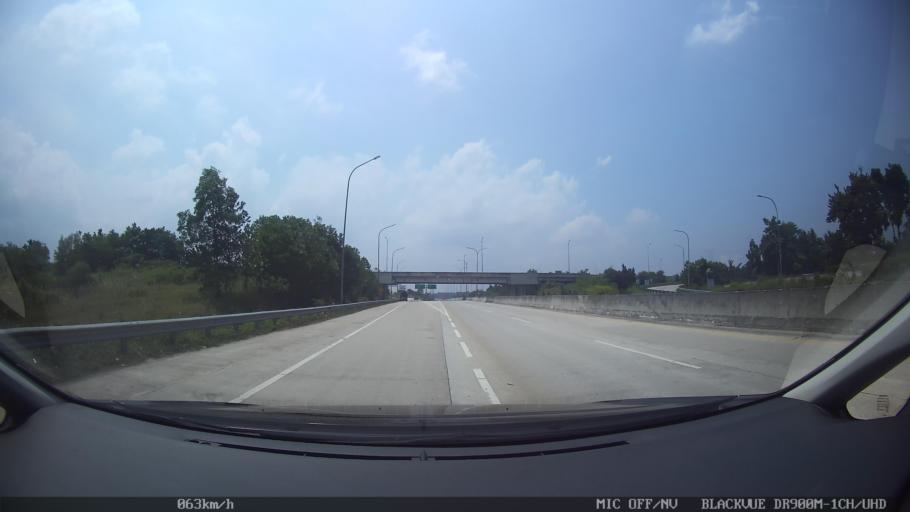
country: ID
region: Lampung
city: Panjang
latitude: -5.3942
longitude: 105.3479
